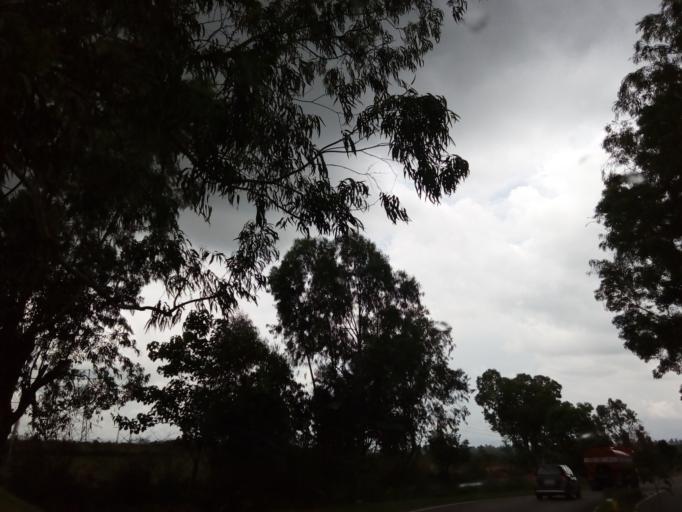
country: IN
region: Karnataka
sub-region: Hassan
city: Belur
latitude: 13.1607
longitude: 75.9006
